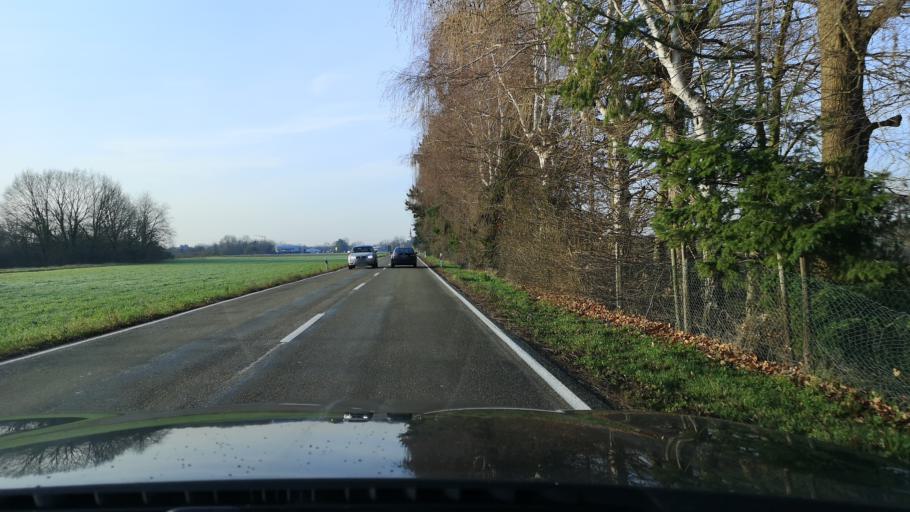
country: DE
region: Rheinland-Pfalz
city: Berg
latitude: 48.9834
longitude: 8.1926
